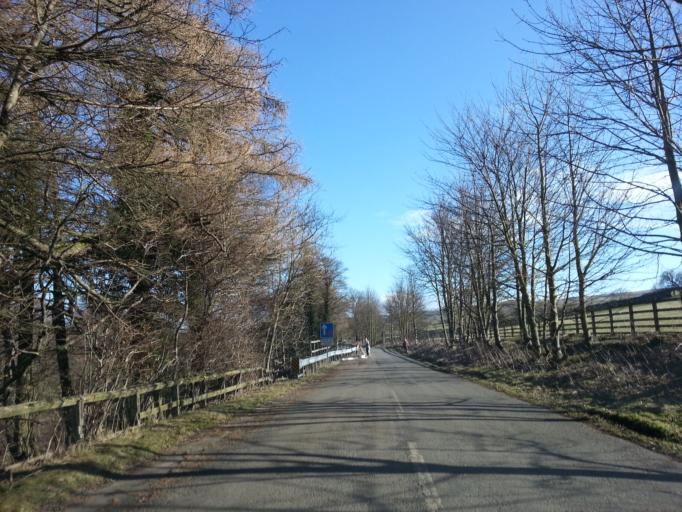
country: GB
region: England
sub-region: County Durham
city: Stanhope
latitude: 54.7272
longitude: -1.9771
